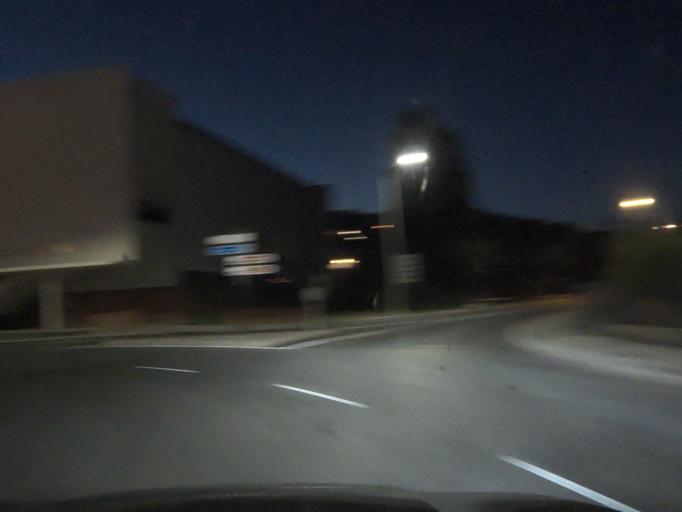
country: PT
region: Faro
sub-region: Loule
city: Loule
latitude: 37.1464
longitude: -8.0116
